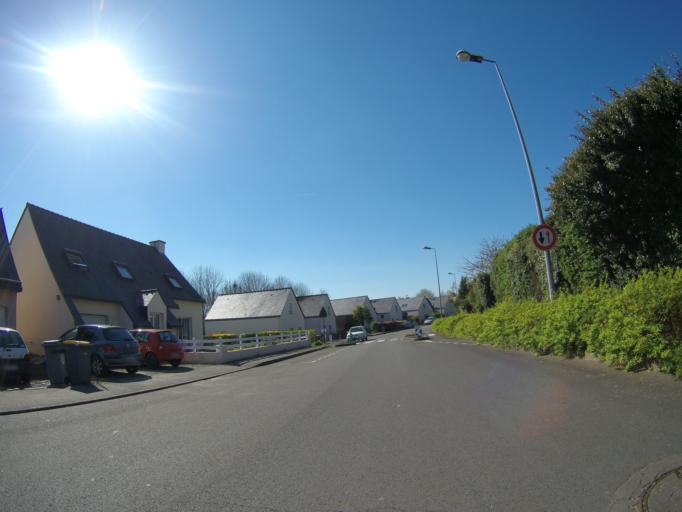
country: FR
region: Brittany
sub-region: Departement d'Ille-et-Vilaine
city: Vern-sur-Seiche
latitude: 48.0470
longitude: -1.6157
